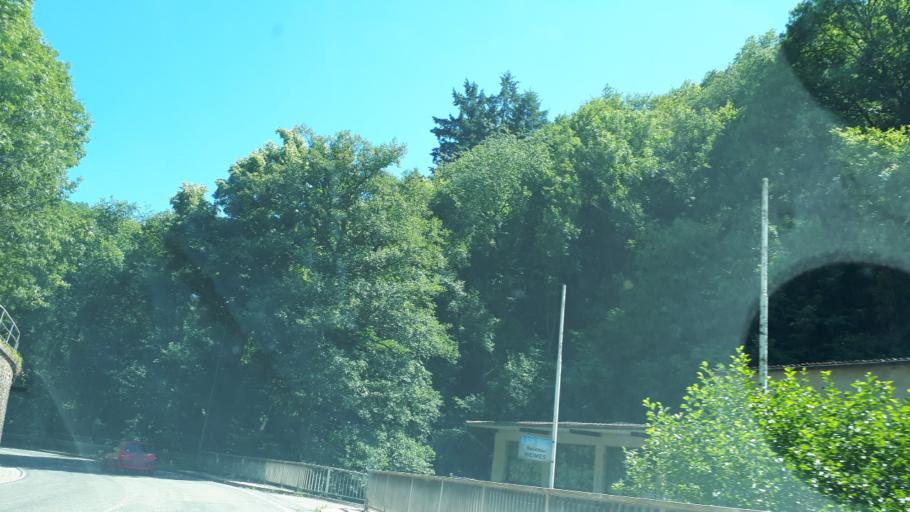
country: DE
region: Rheinland-Pfalz
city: Cochem
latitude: 50.1566
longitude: 7.1484
